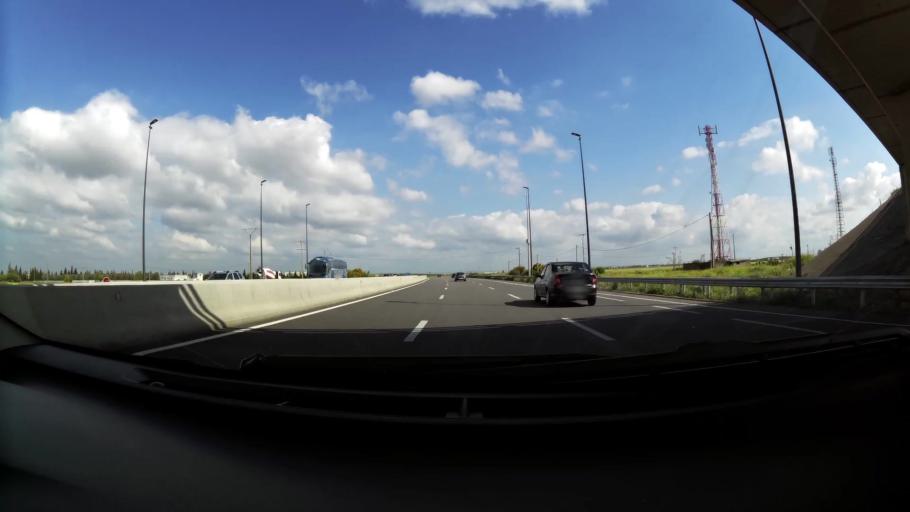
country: MA
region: Chaouia-Ouardigha
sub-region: Settat Province
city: Berrechid
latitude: 33.3170
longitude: -7.6018
